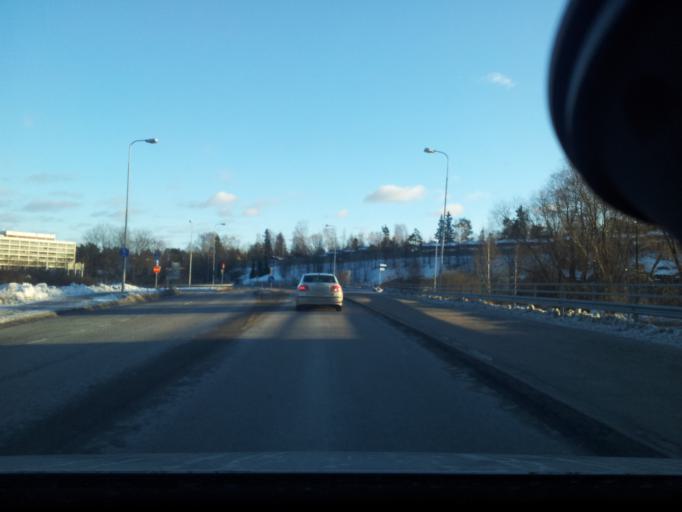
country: FI
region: Uusimaa
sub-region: Helsinki
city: Koukkuniemi
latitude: 60.1684
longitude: 24.7671
